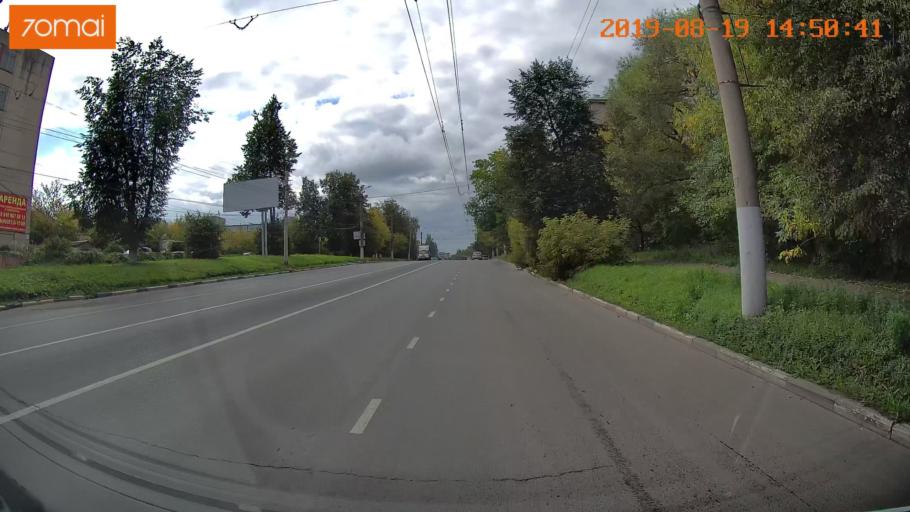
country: RU
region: Ivanovo
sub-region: Gorod Ivanovo
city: Ivanovo
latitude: 56.9942
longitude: 41.0101
